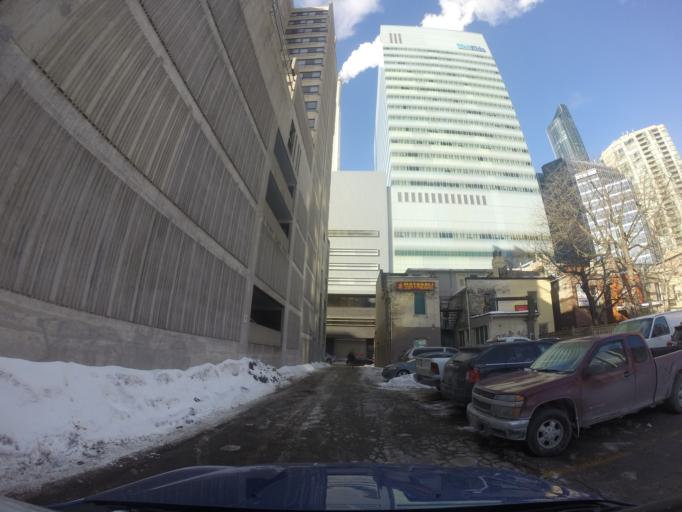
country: CA
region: Ontario
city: Toronto
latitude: 43.6567
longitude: -79.3848
